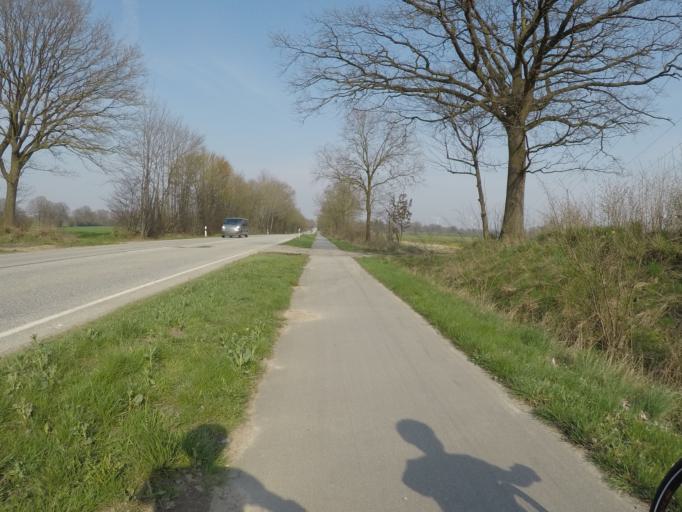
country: DE
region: Schleswig-Holstein
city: Seth
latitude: 53.8333
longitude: 10.2144
